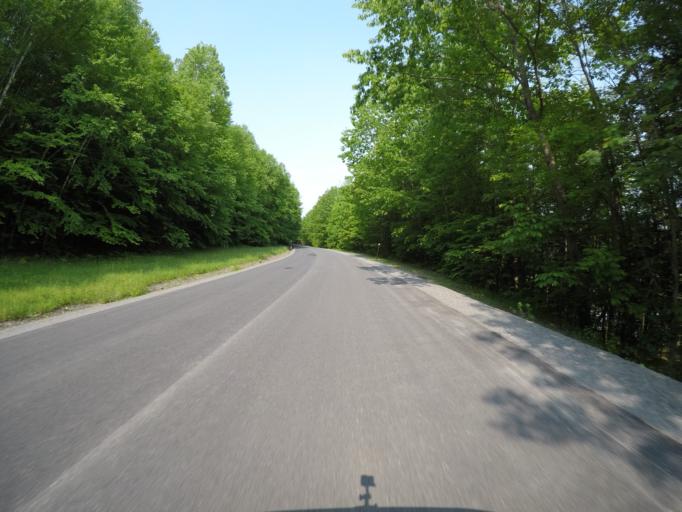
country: US
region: New York
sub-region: Sullivan County
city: Livingston Manor
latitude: 42.1237
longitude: -74.6945
